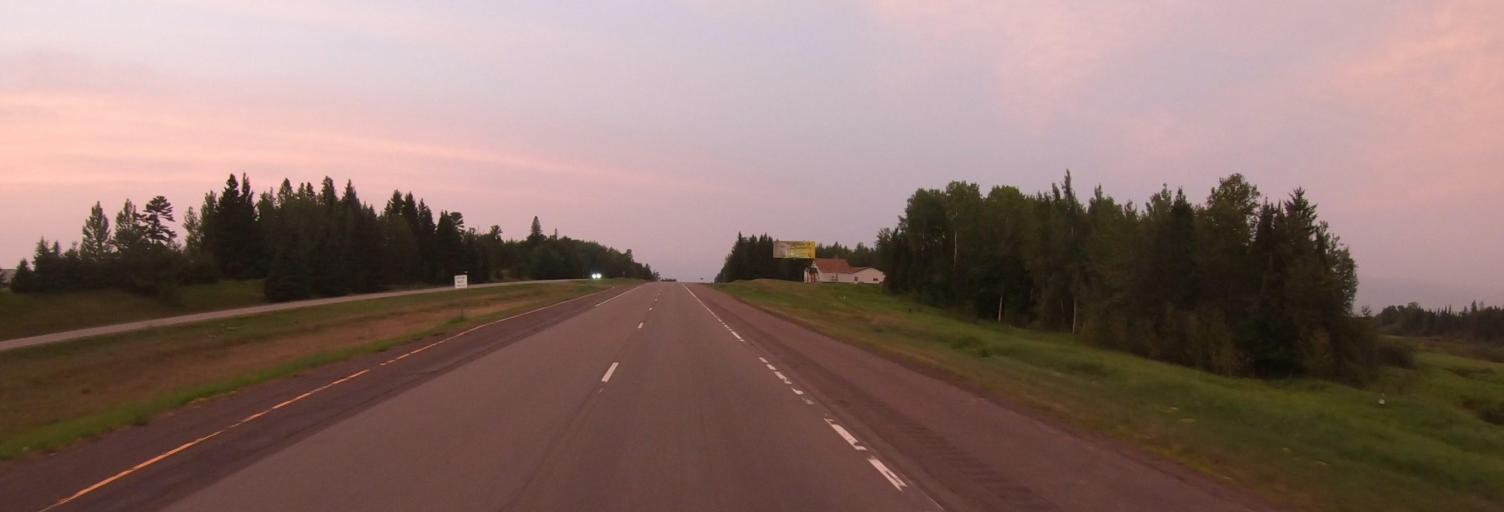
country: US
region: Minnesota
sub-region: Carlton County
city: Cloquet
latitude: 47.0299
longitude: -92.4708
